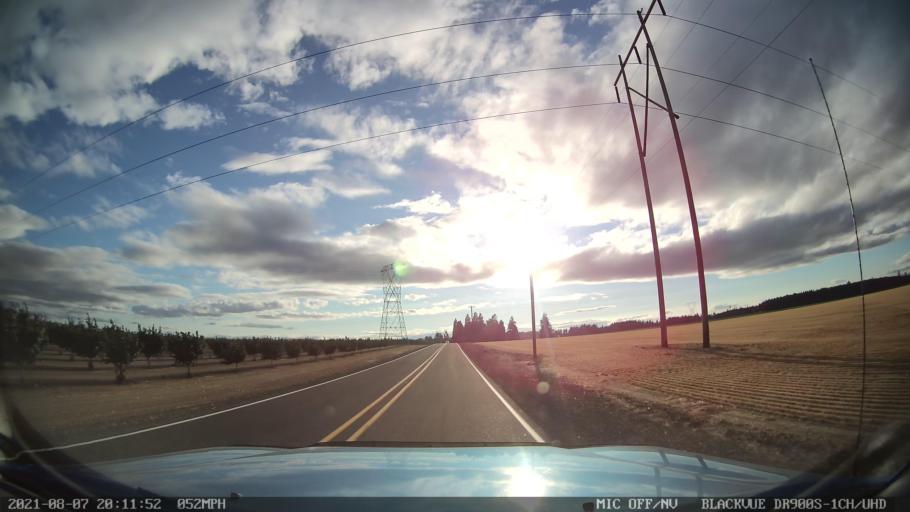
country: US
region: Oregon
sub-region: Marion County
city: Hayesville
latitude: 44.9583
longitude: -122.8978
